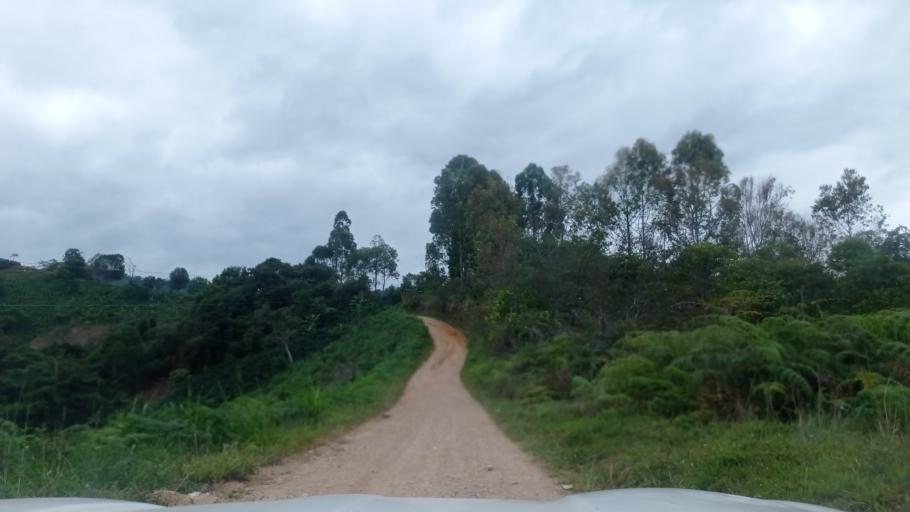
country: CO
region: Huila
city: Garzon
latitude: 2.0958
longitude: -75.6259
